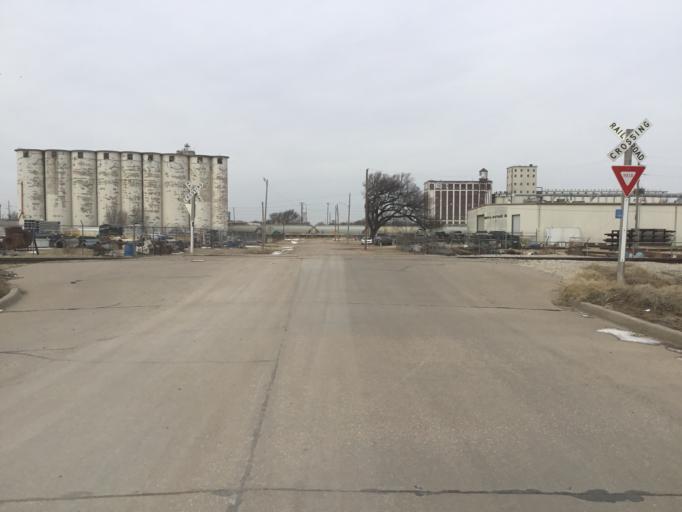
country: US
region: Kansas
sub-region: Sedgwick County
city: Wichita
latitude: 37.7172
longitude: -97.3286
